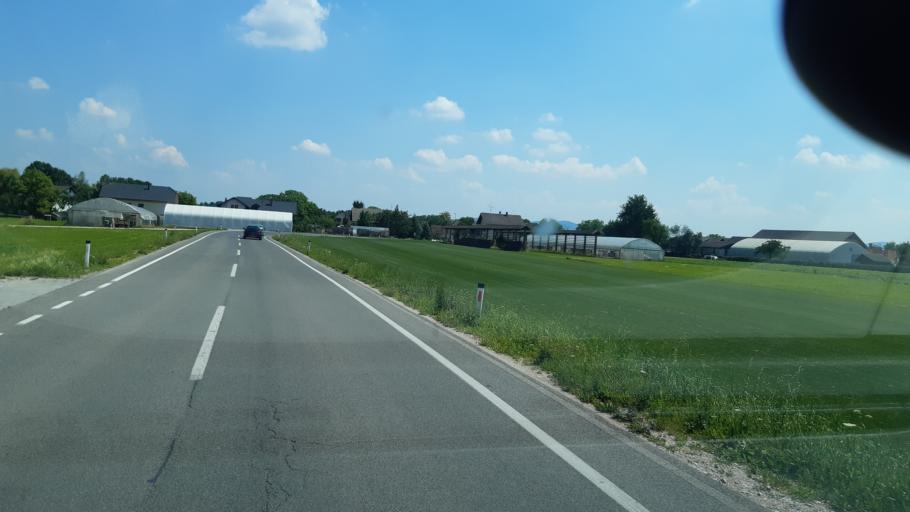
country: SI
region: Cerklje na Gorenjskem
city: Cerklje na Gorenjskem
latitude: 46.2337
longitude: 14.4862
